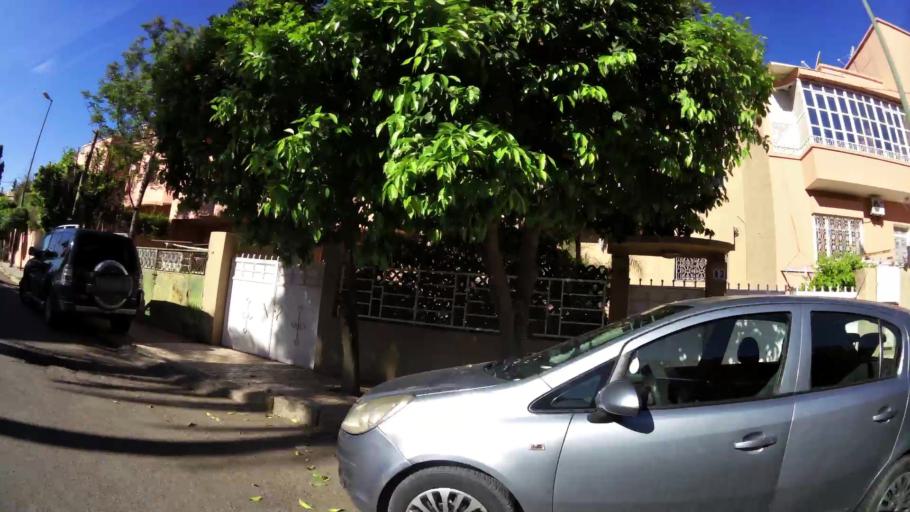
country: MA
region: Marrakech-Tensift-Al Haouz
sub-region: Marrakech
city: Marrakesh
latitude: 31.6456
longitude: -8.0140
